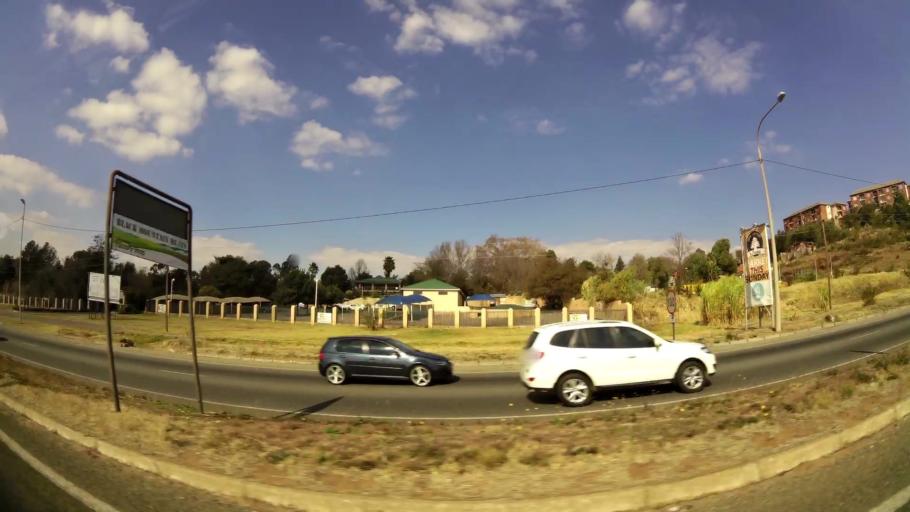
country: ZA
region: Gauteng
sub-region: West Rand District Municipality
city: Krugersdorp
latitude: -26.0737
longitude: 27.7996
